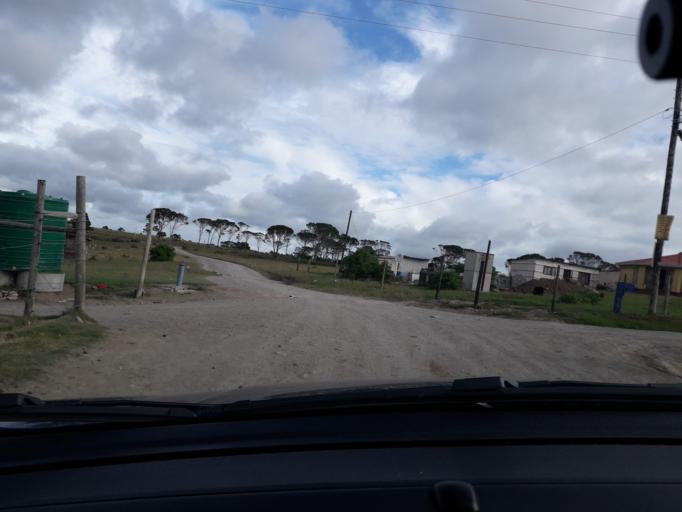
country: ZA
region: Eastern Cape
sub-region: Buffalo City Metropolitan Municipality
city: East London
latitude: -32.8521
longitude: 27.9848
